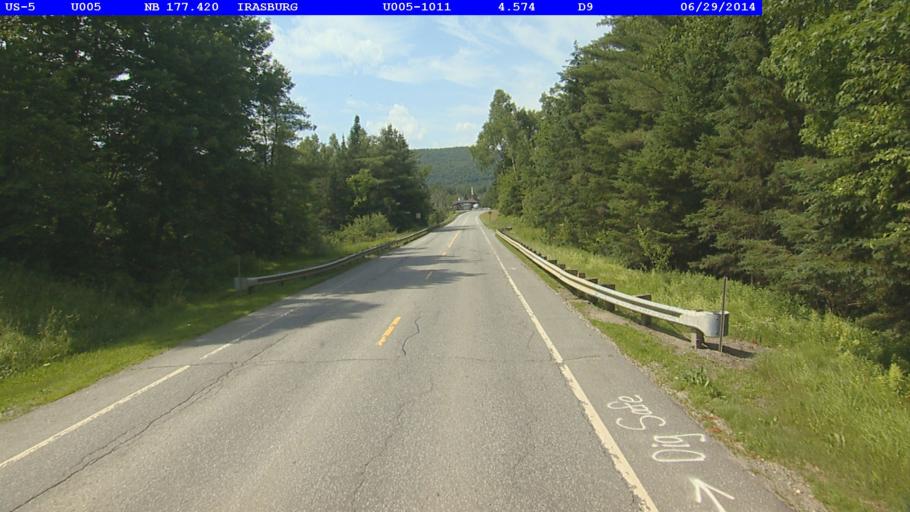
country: US
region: Vermont
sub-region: Orleans County
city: Newport
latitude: 44.8571
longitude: -72.2664
